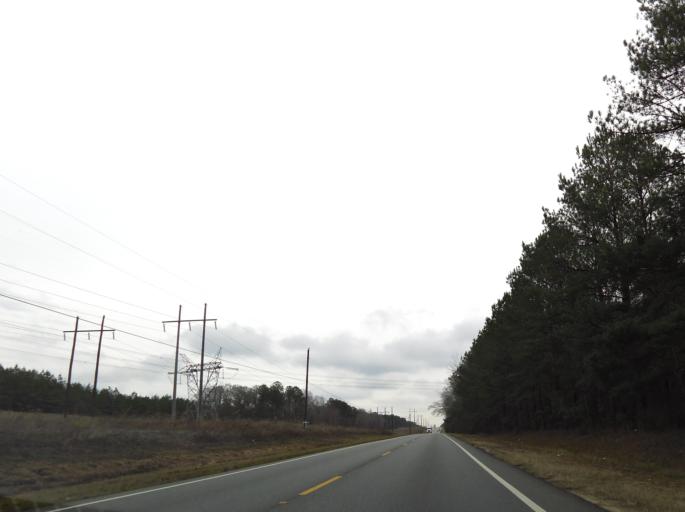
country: US
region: Georgia
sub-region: Houston County
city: Robins Air Force Base
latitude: 32.5418
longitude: -83.5092
